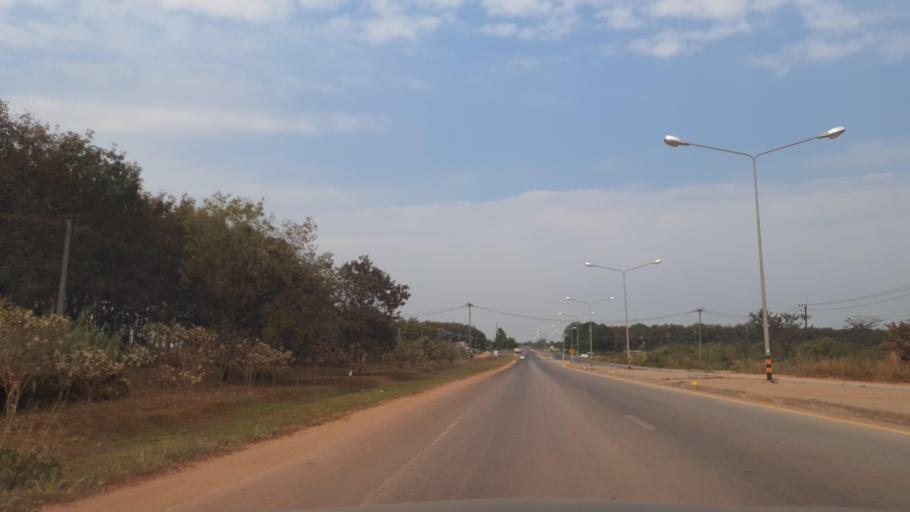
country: TH
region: Changwat Bueng Kan
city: Si Wilai
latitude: 18.2965
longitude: 103.8188
